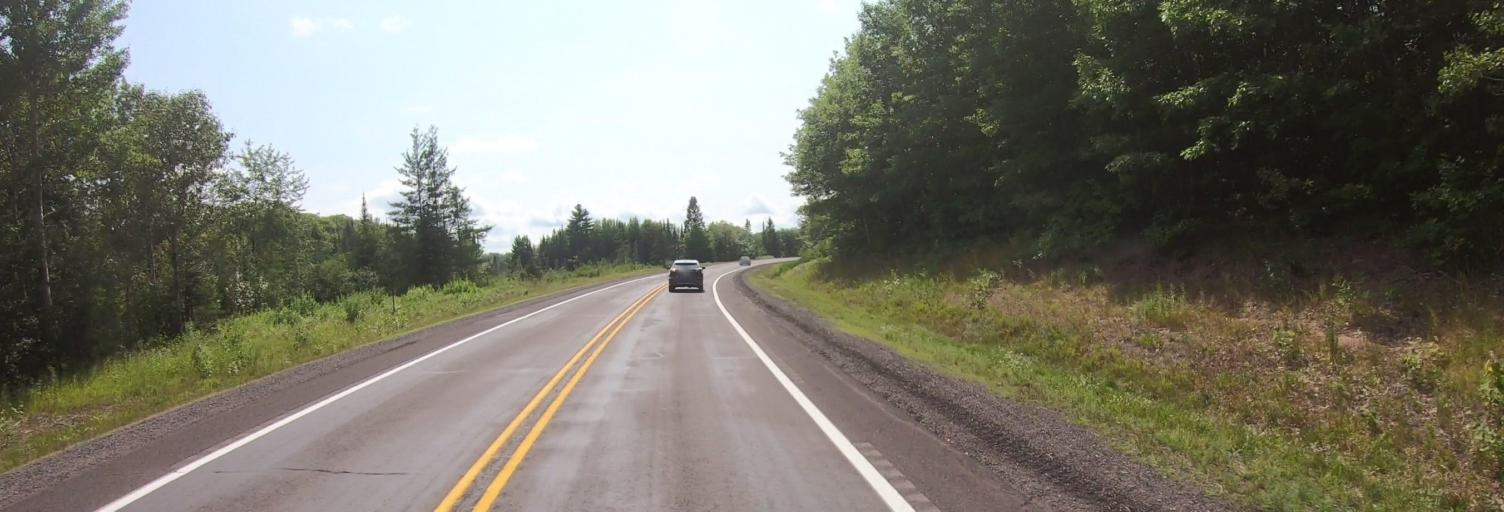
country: US
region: Michigan
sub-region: Houghton County
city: Hancock
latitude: 46.8721
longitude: -88.8752
